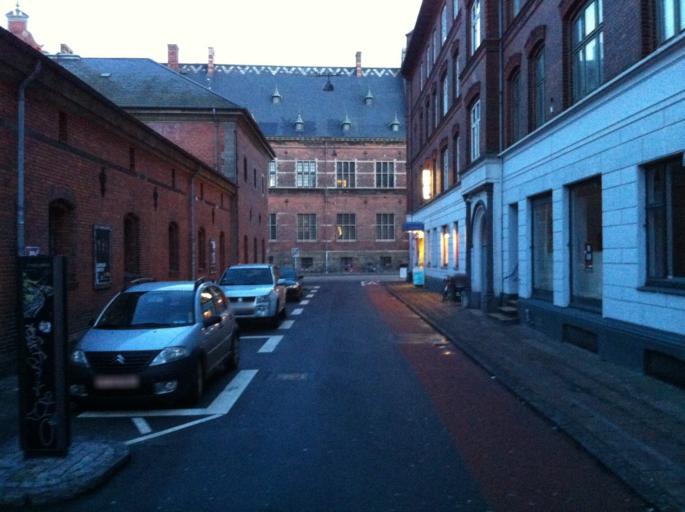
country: DK
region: Capital Region
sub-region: Helsingor Kommune
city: Helsingor
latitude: 56.0340
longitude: 12.6133
